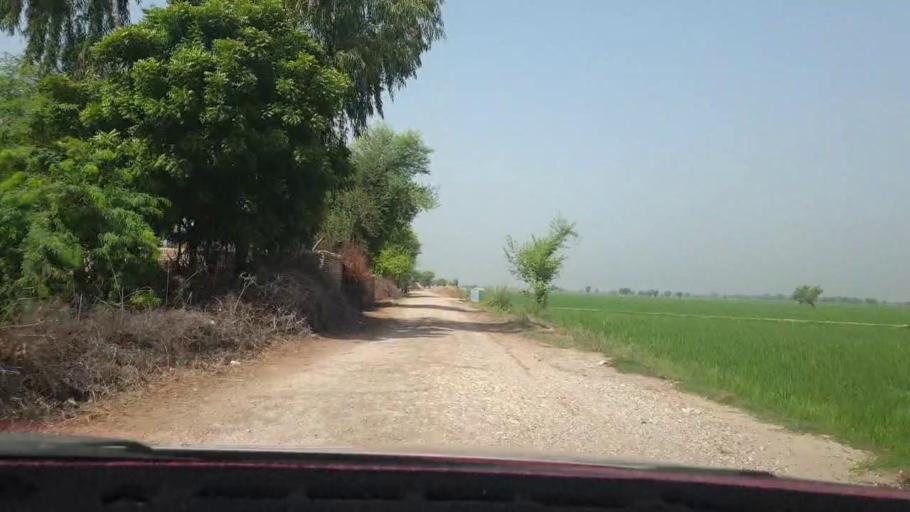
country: PK
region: Sindh
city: Nasirabad
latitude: 27.4301
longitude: 67.8765
